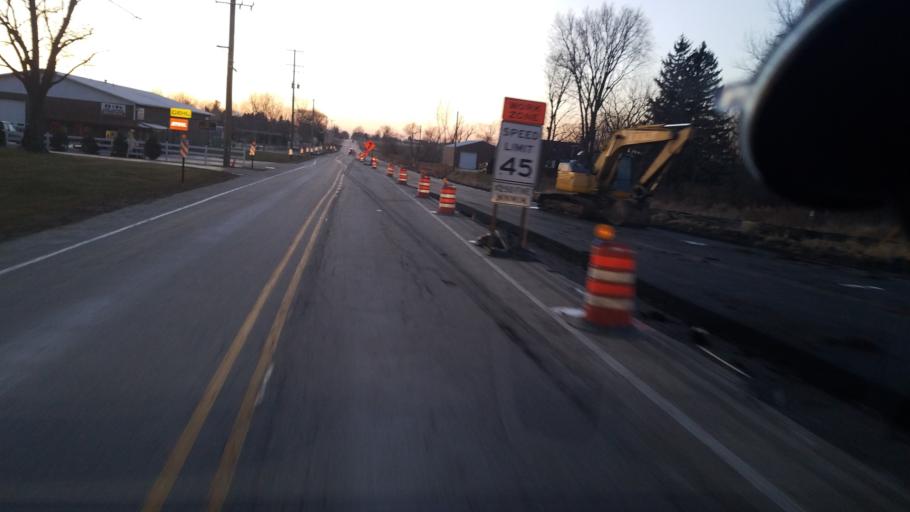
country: US
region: Illinois
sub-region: Kane County
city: Hampshire
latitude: 42.1609
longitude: -88.5278
